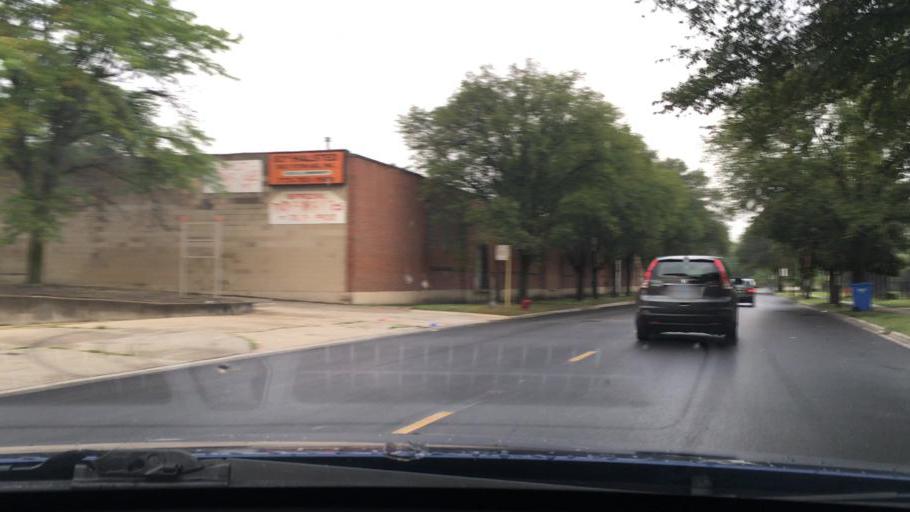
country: US
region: Illinois
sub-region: Cook County
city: Evergreen Park
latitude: 41.7418
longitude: -87.6391
